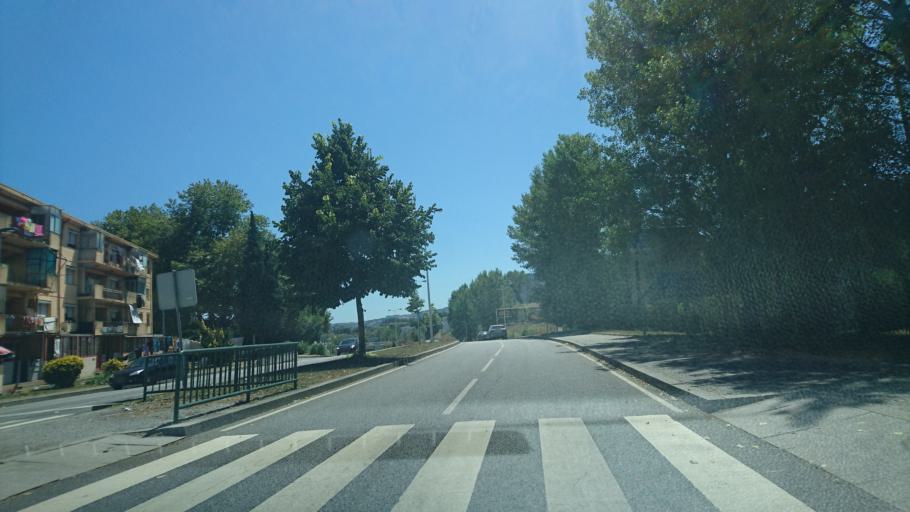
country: PT
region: Porto
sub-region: Gondomar
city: Valbom
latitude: 41.1588
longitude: -8.5720
